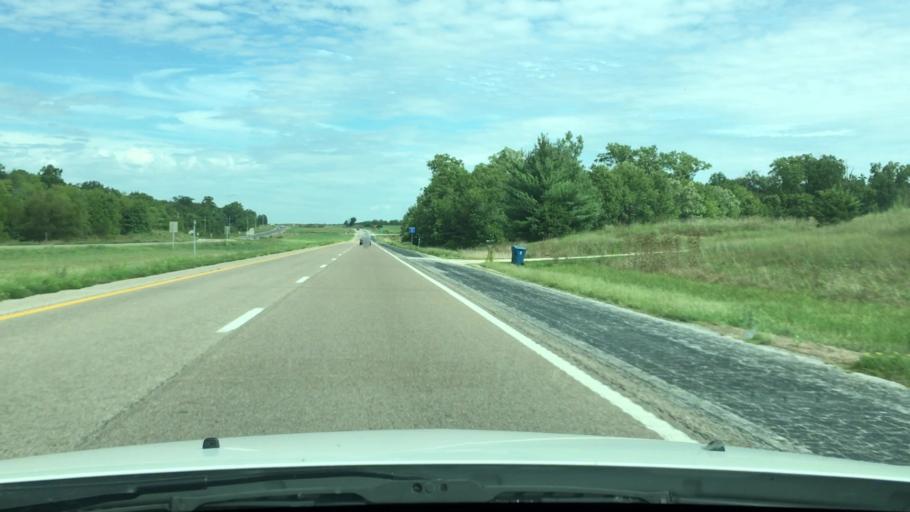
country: US
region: Missouri
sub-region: Audrain County
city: Mexico
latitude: 39.0566
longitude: -91.8944
